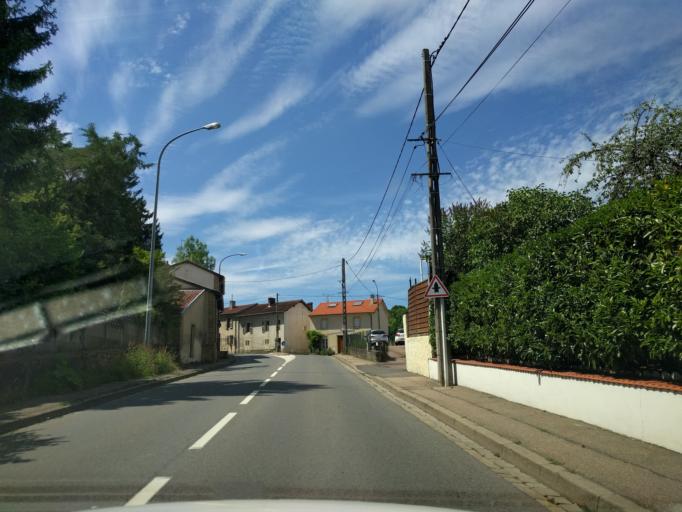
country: FR
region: Lorraine
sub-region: Departement de la Moselle
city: Woippy
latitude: 49.1368
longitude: 6.1465
